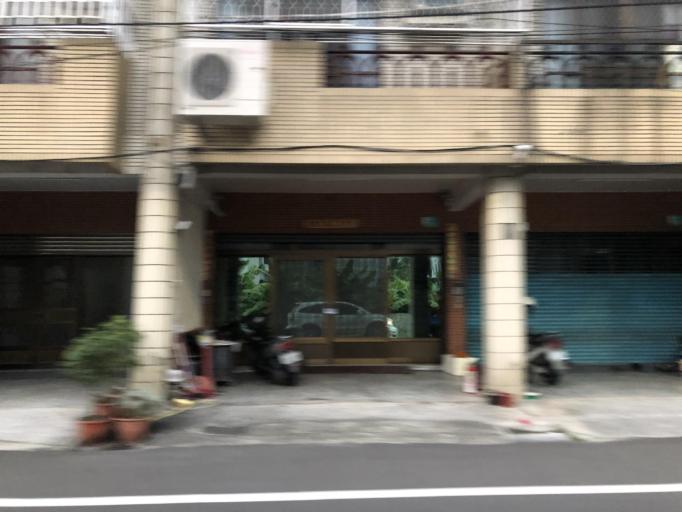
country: TW
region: Taiwan
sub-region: Tainan
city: Tainan
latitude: 23.0208
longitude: 120.2781
